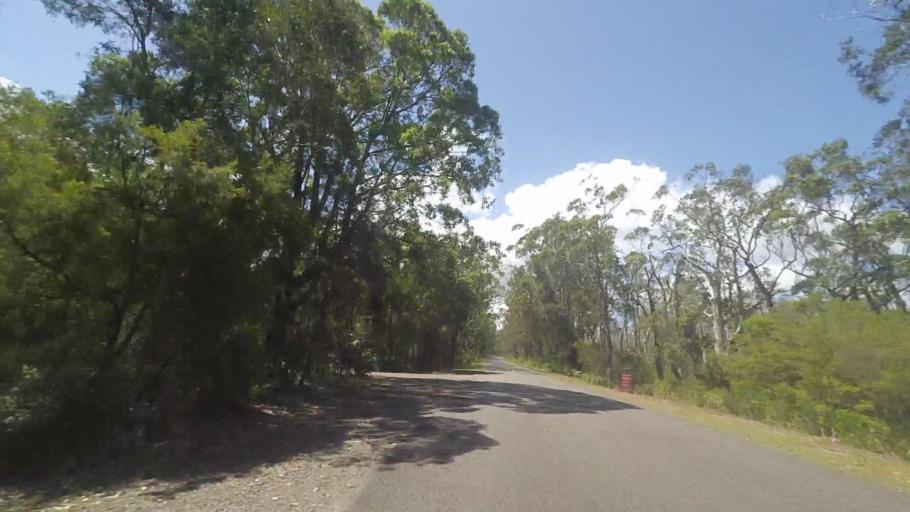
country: AU
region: New South Wales
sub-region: Great Lakes
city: Bulahdelah
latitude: -32.5251
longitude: 152.3229
